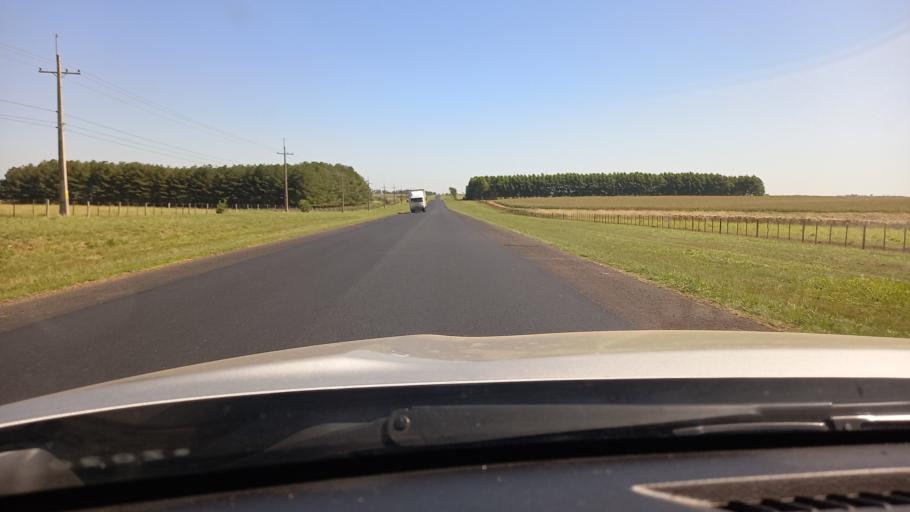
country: PY
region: Misiones
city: San Patricio
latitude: -26.9993
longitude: -56.7631
